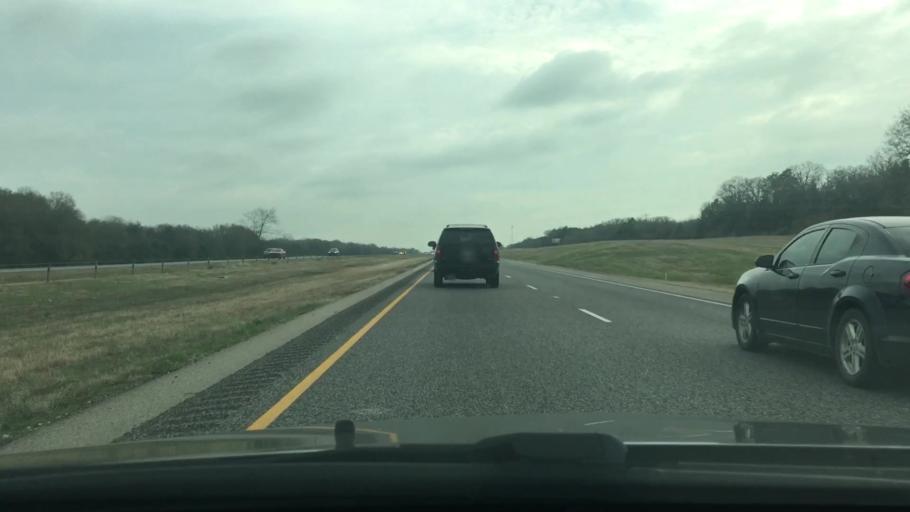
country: US
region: Texas
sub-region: Freestone County
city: Fairfield
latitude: 31.6223
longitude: -96.1575
